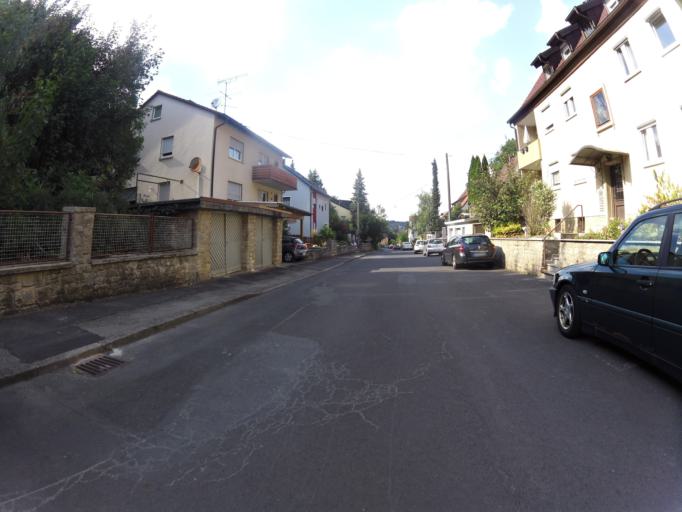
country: DE
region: Bavaria
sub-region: Regierungsbezirk Unterfranken
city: Ochsenfurt
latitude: 49.6590
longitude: 10.0599
